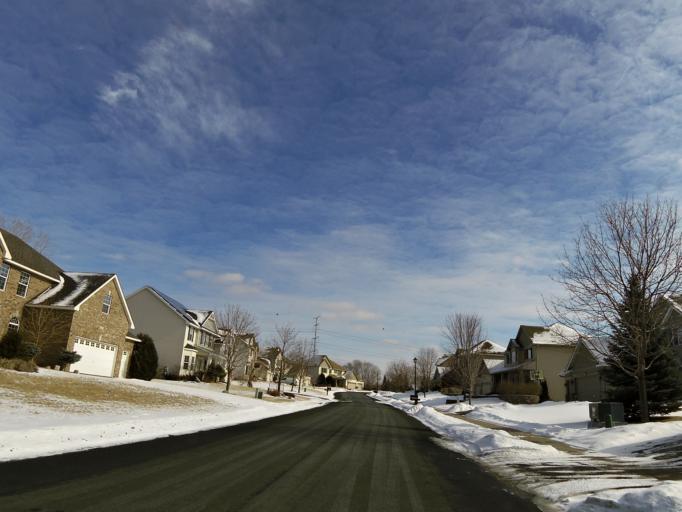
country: US
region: Minnesota
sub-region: Hennepin County
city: Eden Prairie
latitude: 44.8213
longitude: -93.4332
